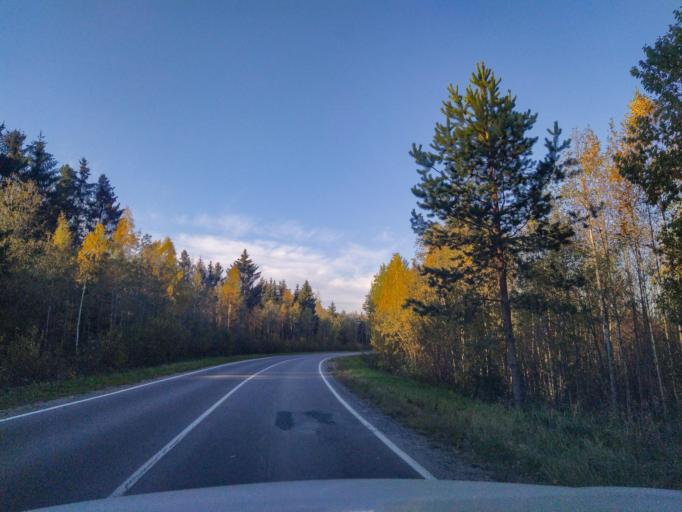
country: RU
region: Leningrad
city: Siverskiy
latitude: 59.3079
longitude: 30.0298
